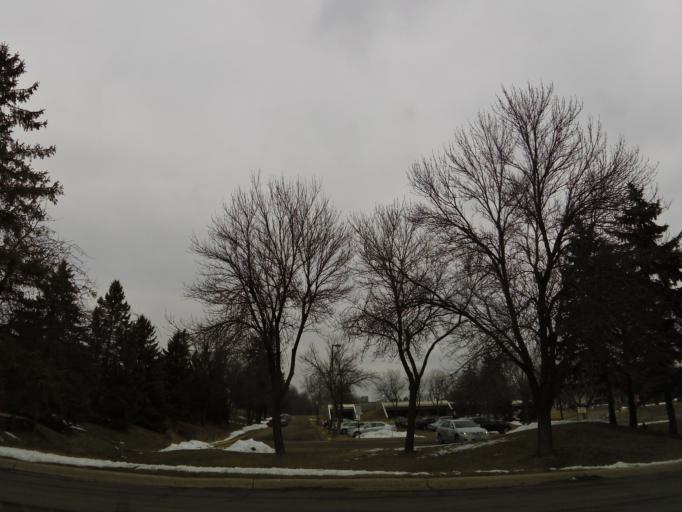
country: US
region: Minnesota
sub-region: Hennepin County
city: Minnetonka Mills
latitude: 44.8993
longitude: -93.4220
